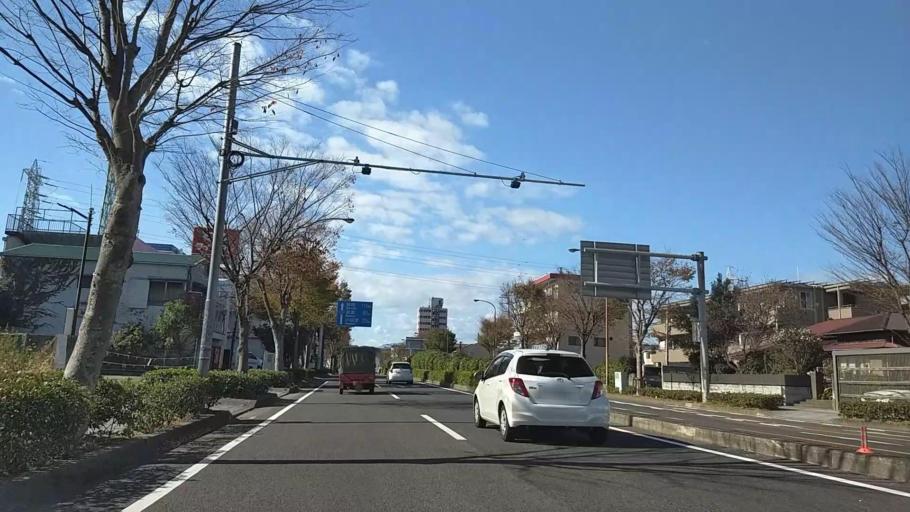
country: JP
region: Kanagawa
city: Hiratsuka
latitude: 35.3316
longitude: 139.3391
